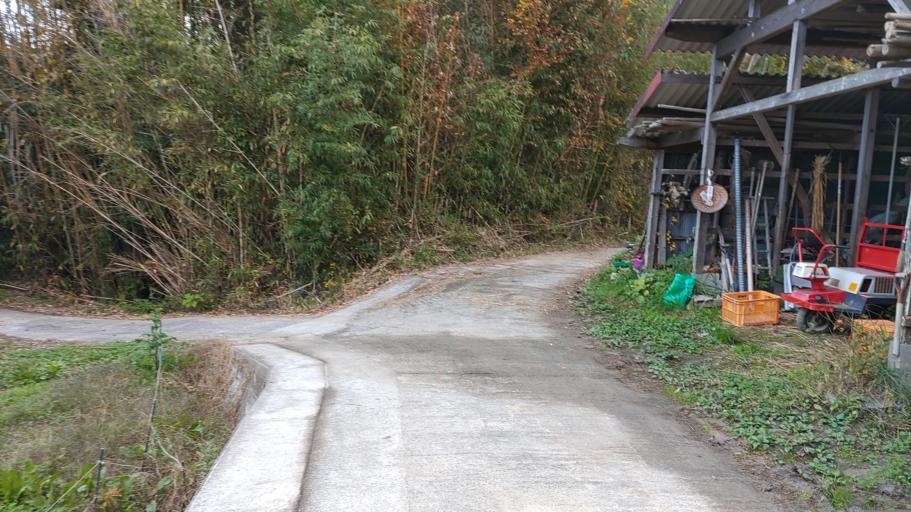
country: JP
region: Hyogo
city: Sumoto
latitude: 34.3825
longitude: 134.8179
